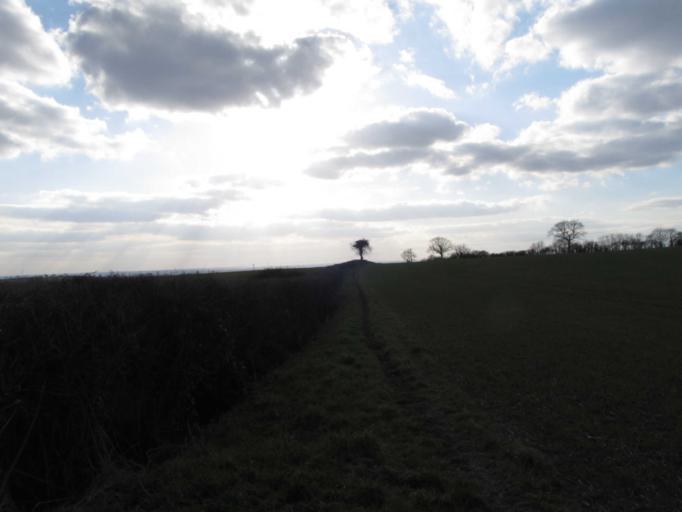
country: GB
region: England
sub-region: Nottinghamshire
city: Misterton
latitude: 53.3921
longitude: -0.8721
